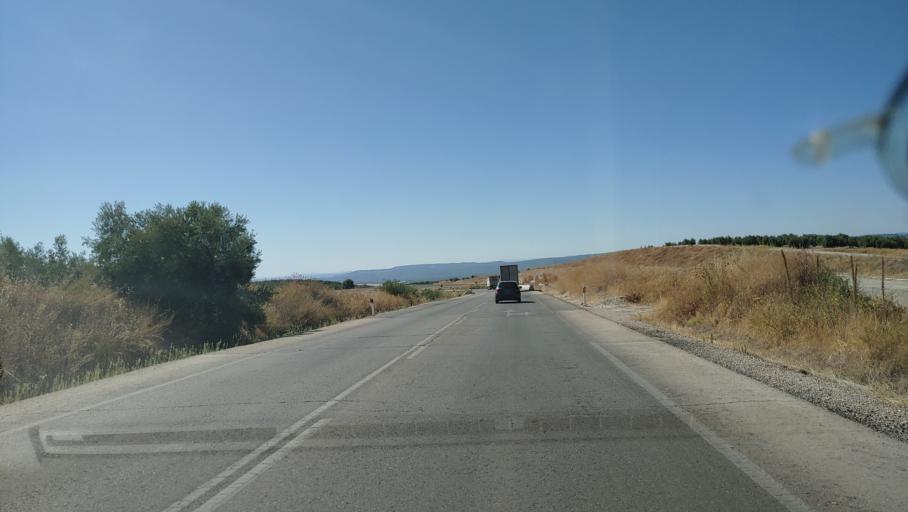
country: ES
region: Andalusia
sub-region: Provincia de Jaen
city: Villacarrillo
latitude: 38.1044
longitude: -3.1135
